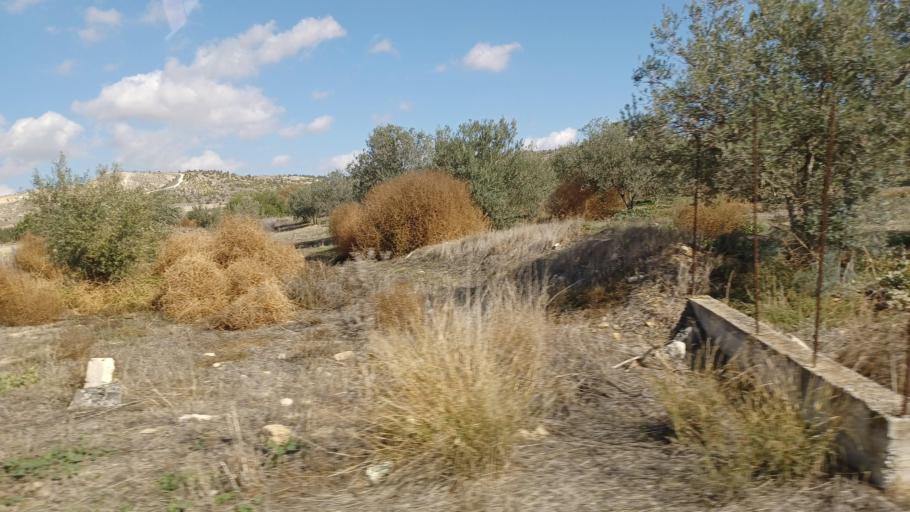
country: CY
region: Larnaka
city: Voroklini
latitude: 35.0060
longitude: 33.6489
